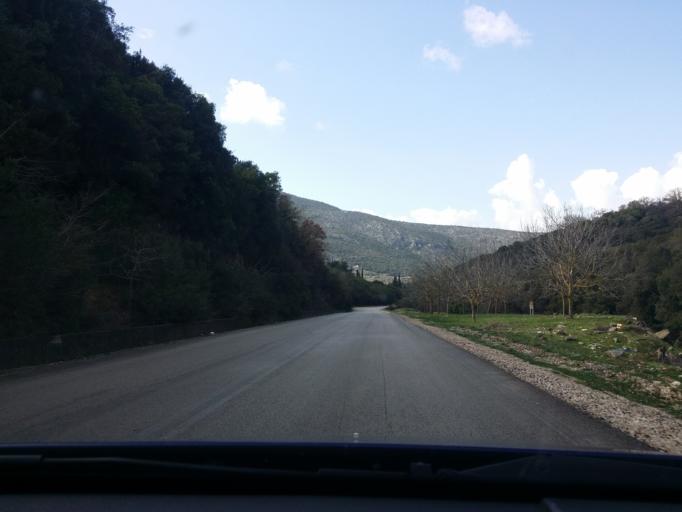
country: GR
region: West Greece
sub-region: Nomos Aitolias kai Akarnanias
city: Astakos
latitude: 38.5984
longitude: 21.1002
